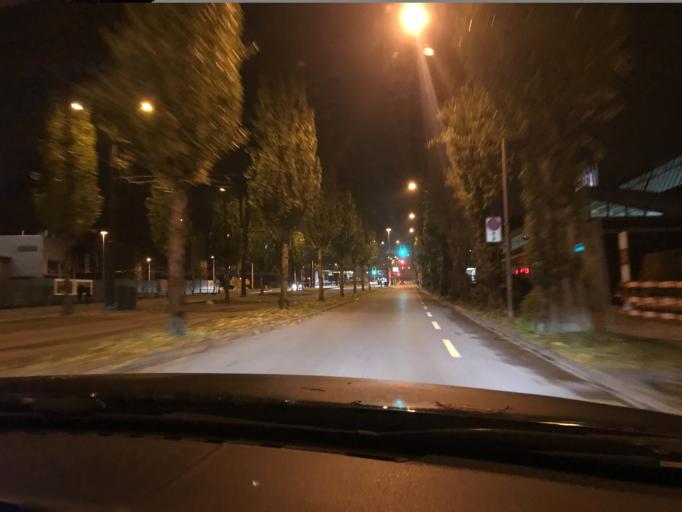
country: CH
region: Zurich
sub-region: Bezirk Zuerich
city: Zuerich (Kreis 11) / Oerlikon
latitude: 47.4123
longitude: 8.5504
